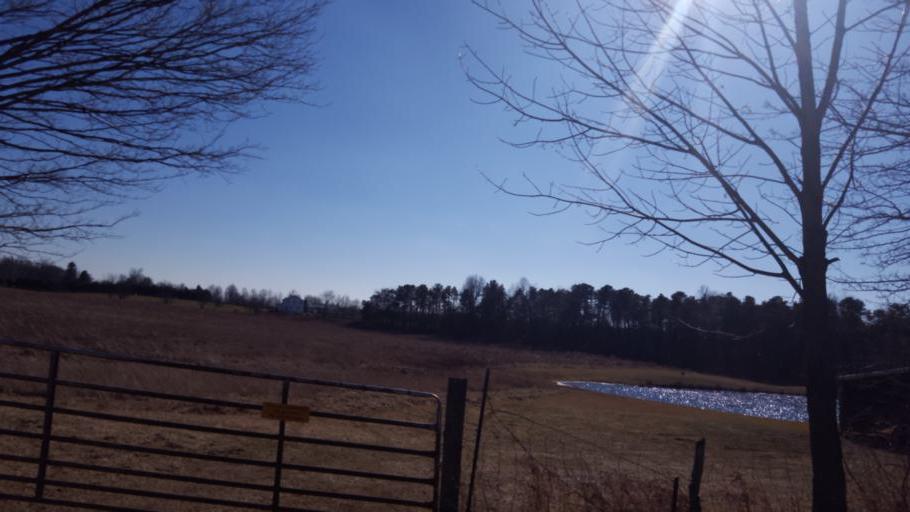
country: US
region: Ohio
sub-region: Sandusky County
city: Bellville
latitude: 40.5749
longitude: -82.5874
